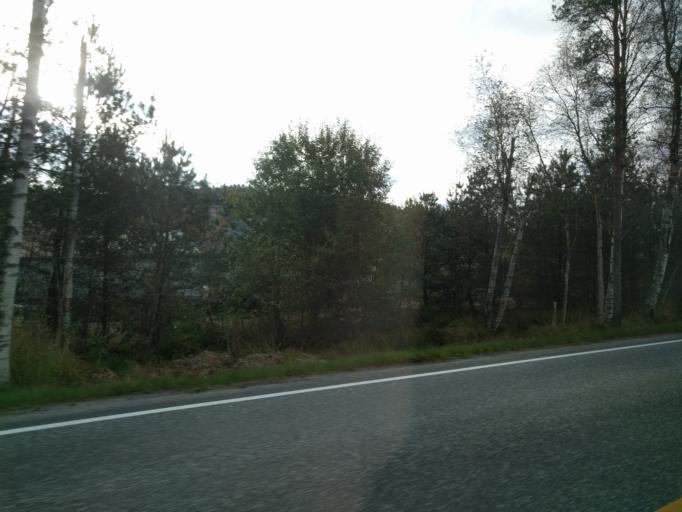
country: NO
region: Vest-Agder
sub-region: Songdalen
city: Nodeland
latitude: 58.2765
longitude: 7.8356
